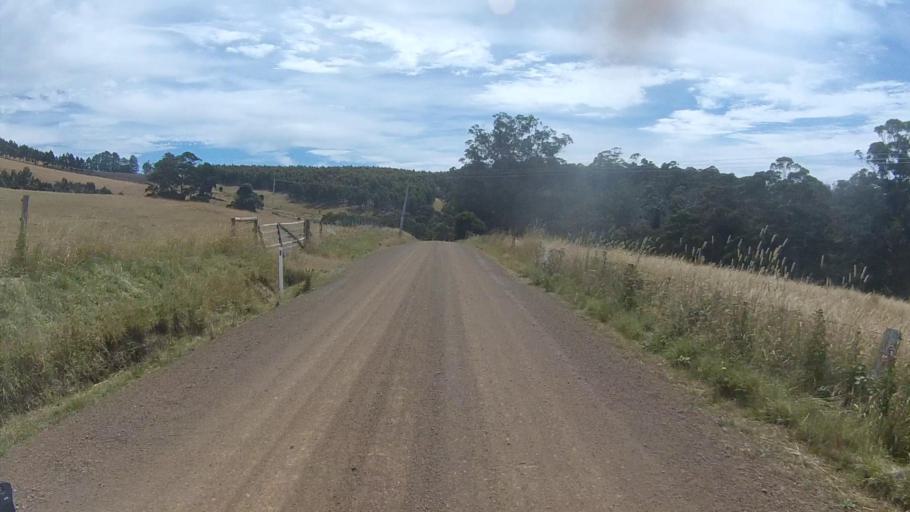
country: AU
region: Tasmania
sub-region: Sorell
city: Sorell
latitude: -42.7882
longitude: 147.8418
